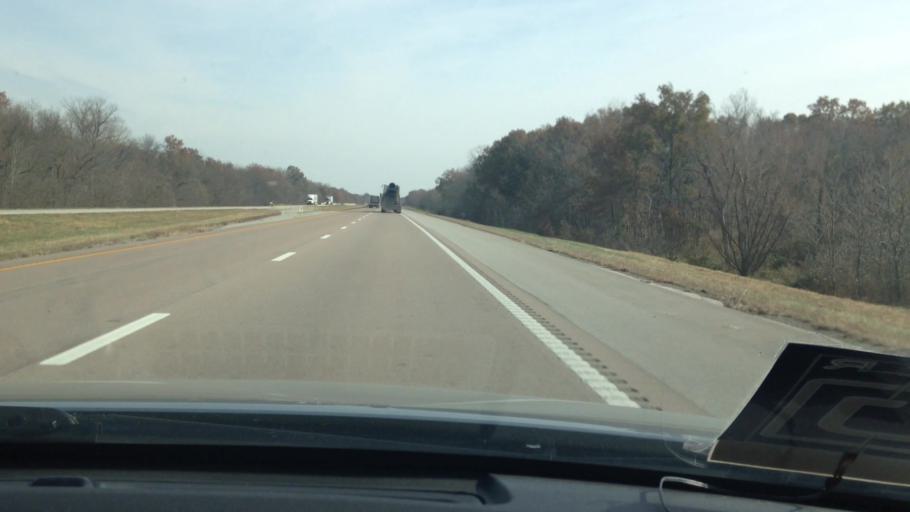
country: US
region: Missouri
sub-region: Henry County
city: Clinton
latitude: 38.4277
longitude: -93.9069
